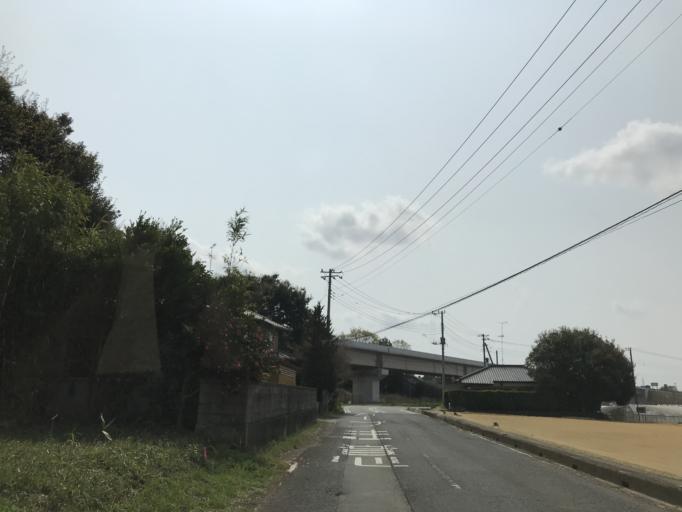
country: JP
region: Ibaraki
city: Naka
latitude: 36.0581
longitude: 140.0780
